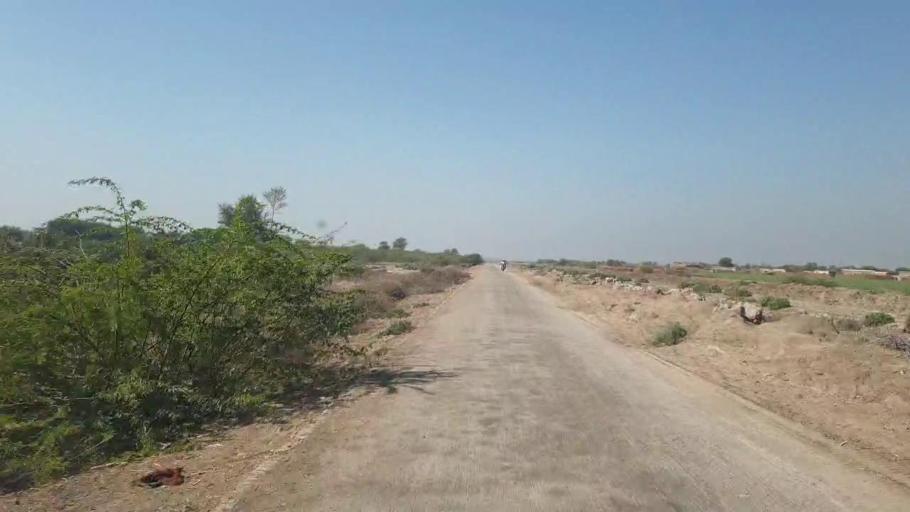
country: PK
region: Sindh
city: Digri
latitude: 25.2710
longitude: 69.2108
